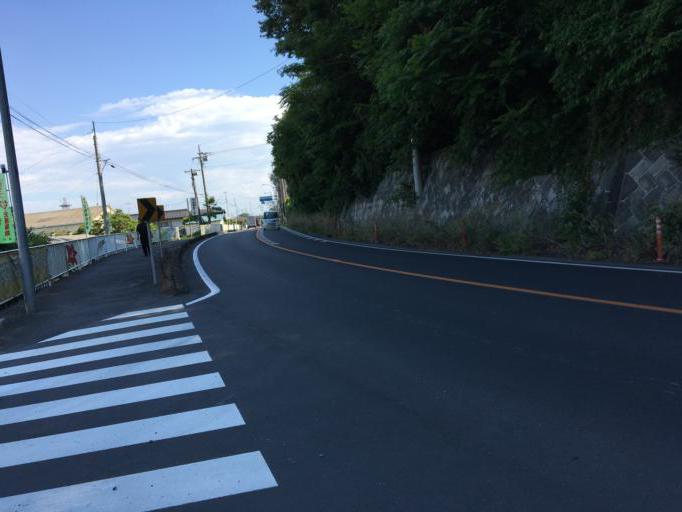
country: JP
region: Saitama
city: Morohongo
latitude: 35.9829
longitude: 139.3341
